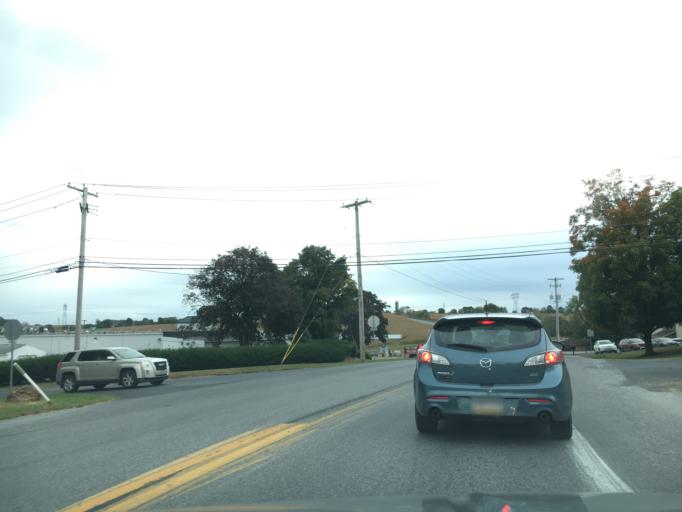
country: US
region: Pennsylvania
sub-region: Lancaster County
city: Quarryville
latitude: 39.8718
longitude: -76.2257
